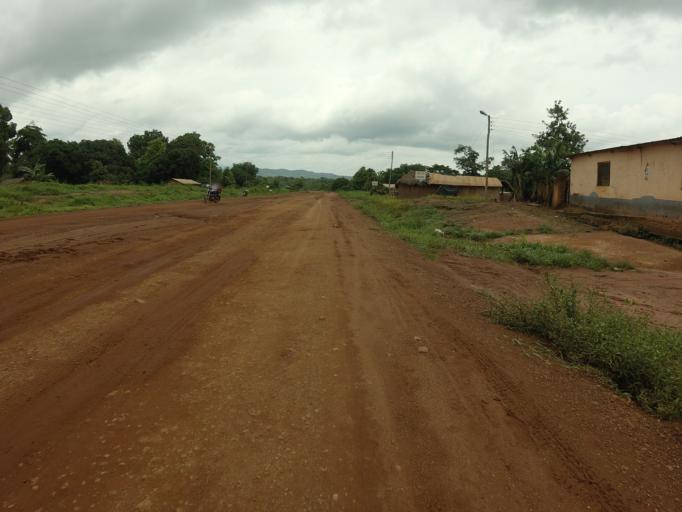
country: GH
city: Kpandae
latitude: 8.2999
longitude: 0.4864
